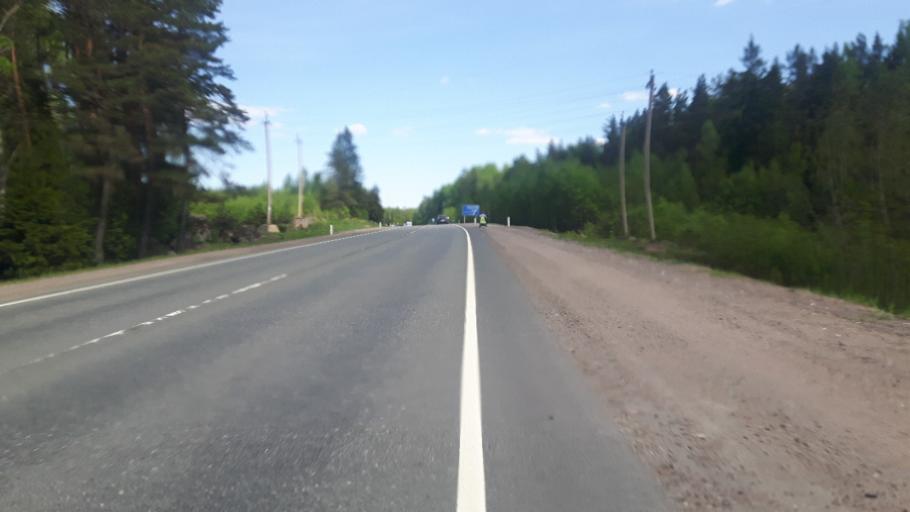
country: RU
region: Leningrad
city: Vyborg
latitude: 60.7440
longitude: 28.6603
